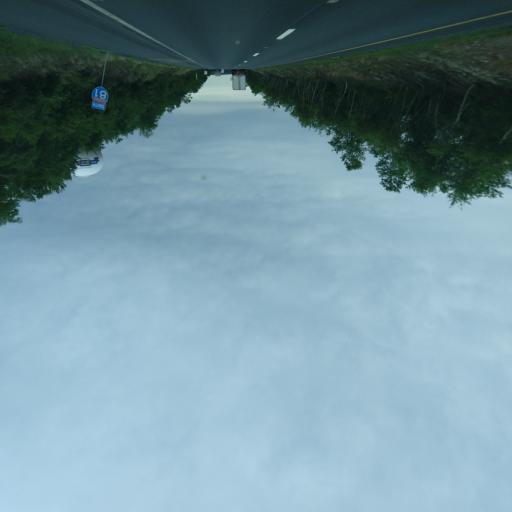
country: US
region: Pennsylvania
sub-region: Schuylkill County
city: Mahanoy City
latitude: 40.8053
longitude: -76.1120
